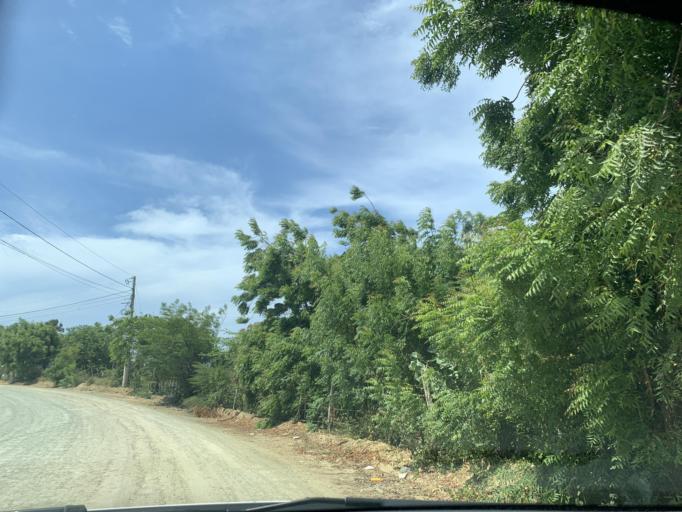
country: DO
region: Puerto Plata
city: Imbert
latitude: 19.8700
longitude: -70.8214
